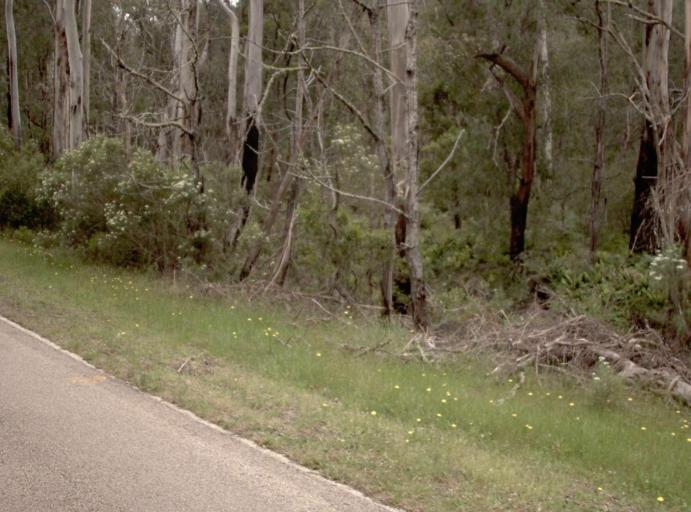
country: AU
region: Victoria
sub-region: East Gippsland
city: Bairnsdale
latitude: -37.6300
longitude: 147.2188
